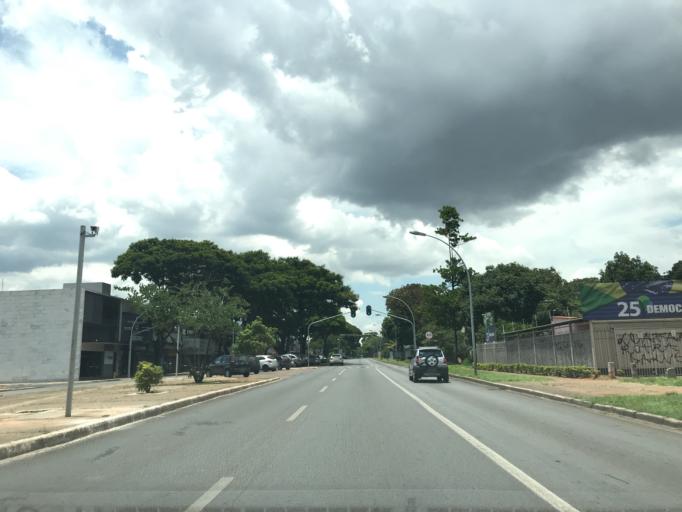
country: BR
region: Federal District
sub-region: Brasilia
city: Brasilia
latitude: -15.8213
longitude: -47.9187
